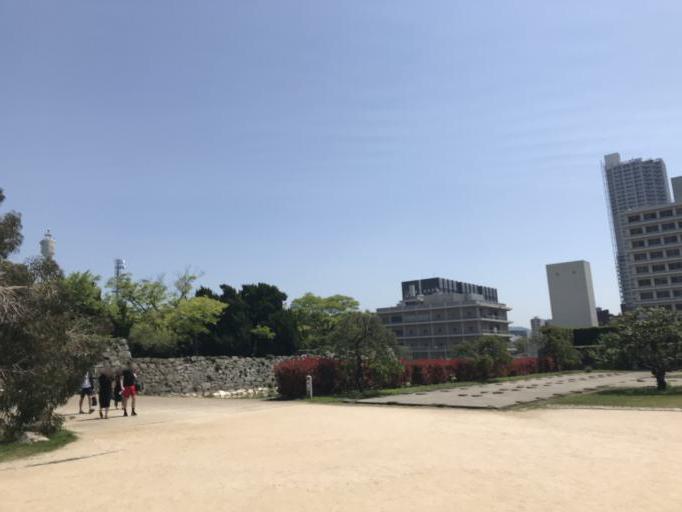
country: JP
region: Hiroshima
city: Hiroshima-shi
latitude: 34.4001
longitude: 132.4593
